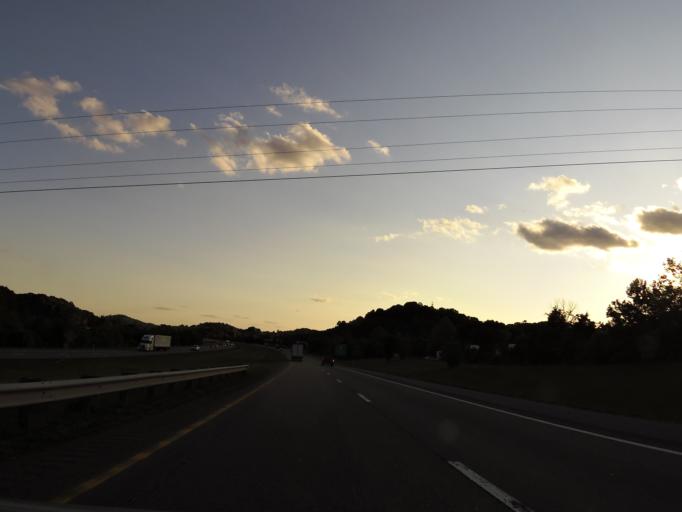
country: US
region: Tennessee
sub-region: Sullivan County
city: Blountville
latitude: 36.5373
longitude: -82.3807
